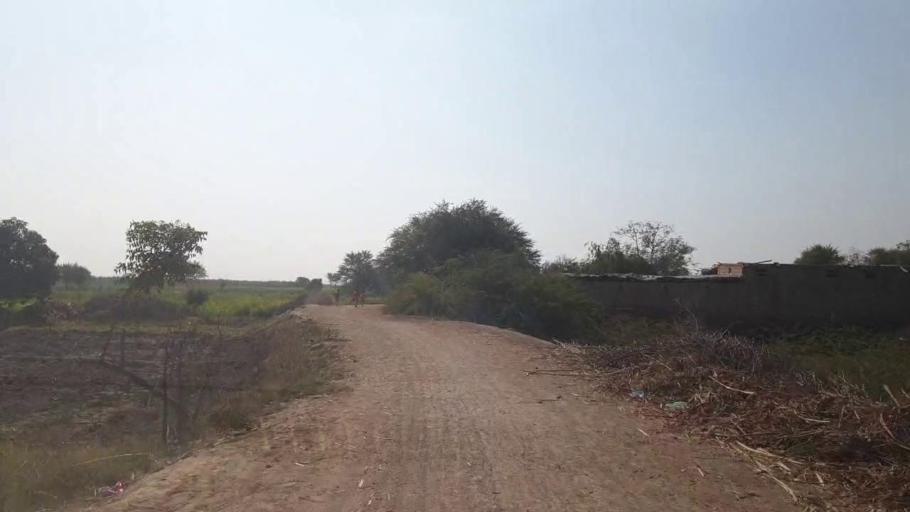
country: PK
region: Sindh
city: Tando Allahyar
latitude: 25.6103
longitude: 68.7403
